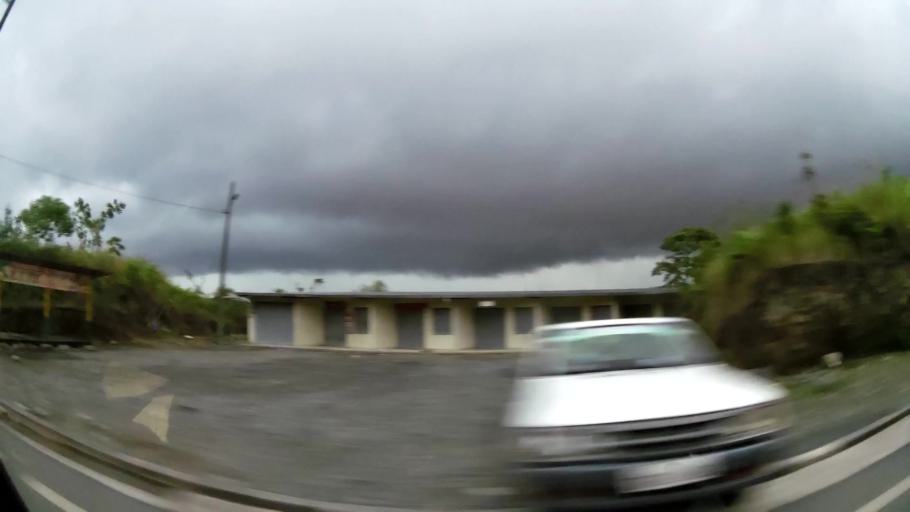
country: EC
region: Pastaza
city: Puyo
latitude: -1.4803
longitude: -78.0091
